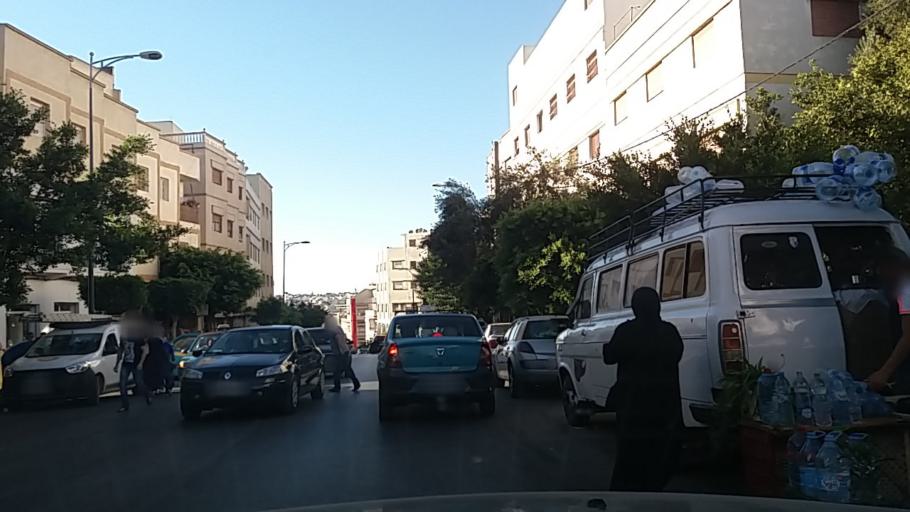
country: MA
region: Tanger-Tetouan
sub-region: Tanger-Assilah
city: Tangier
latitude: 35.7558
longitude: -5.8208
